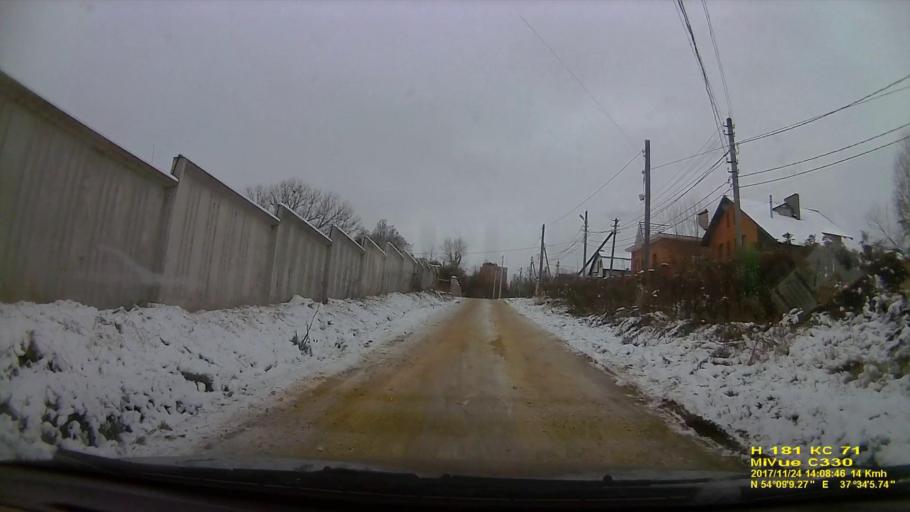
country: RU
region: Tula
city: Mendeleyevskiy
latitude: 54.1525
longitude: 37.5683
